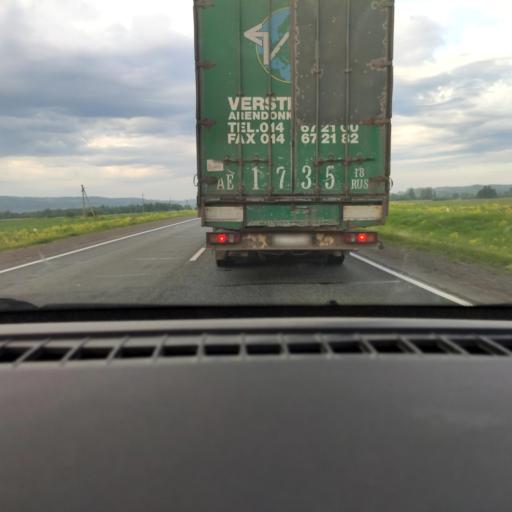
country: RU
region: Perm
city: Chastyye
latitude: 57.4043
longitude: 54.4535
